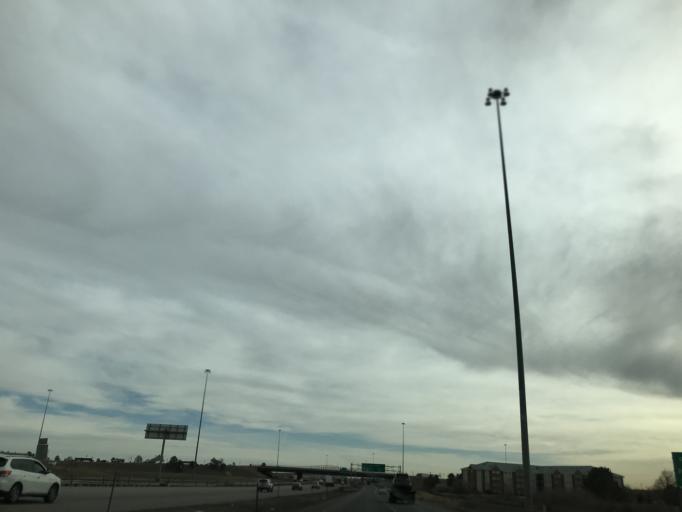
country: US
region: Colorado
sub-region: Adams County
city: Aurora
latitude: 39.7673
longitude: -104.7964
